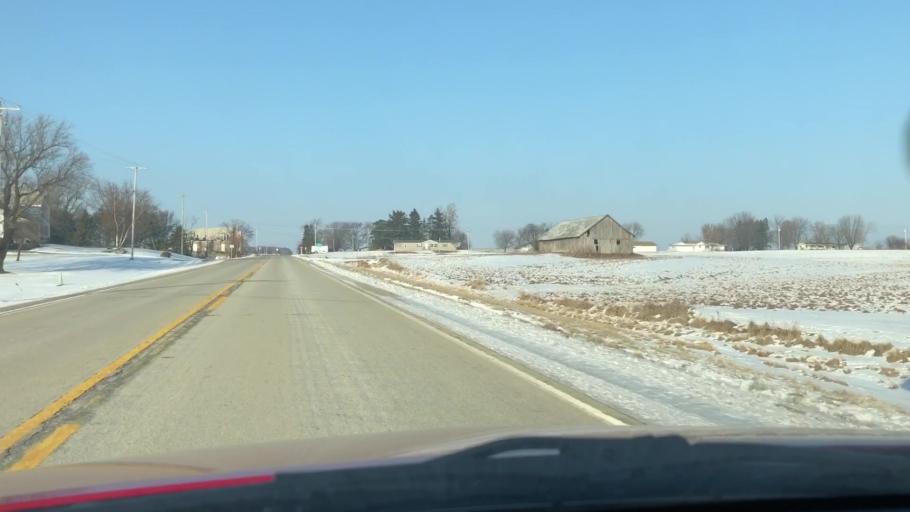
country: US
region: Wisconsin
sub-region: Outagamie County
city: Black Creek
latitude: 44.4121
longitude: -88.3743
